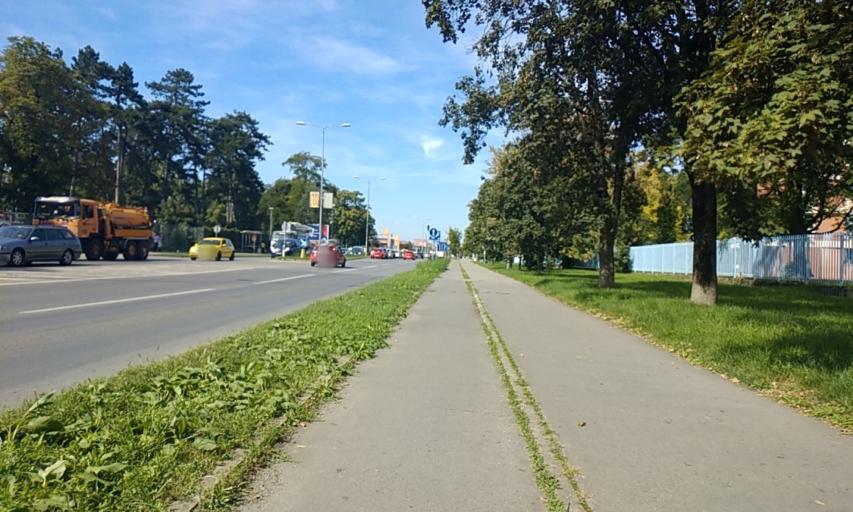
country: BA
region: Republika Srpska
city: Starcevica
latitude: 44.7736
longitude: 17.2084
